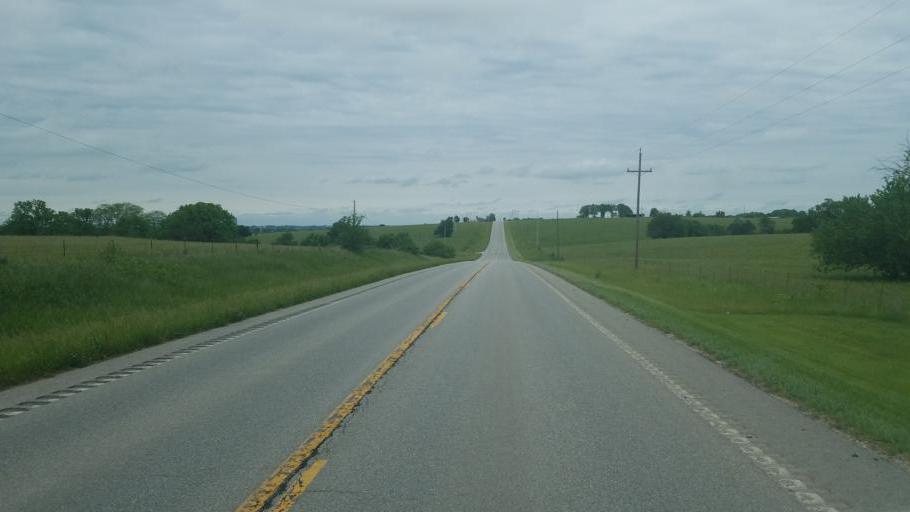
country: US
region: Missouri
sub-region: Morgan County
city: Versailles
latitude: 38.4871
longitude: -92.8084
